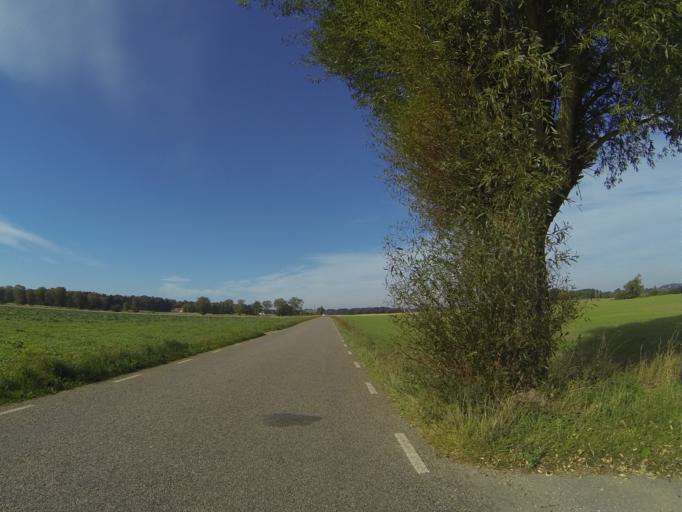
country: SE
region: Skane
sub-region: Eslovs Kommun
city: Eslov
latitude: 55.7316
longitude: 13.3772
